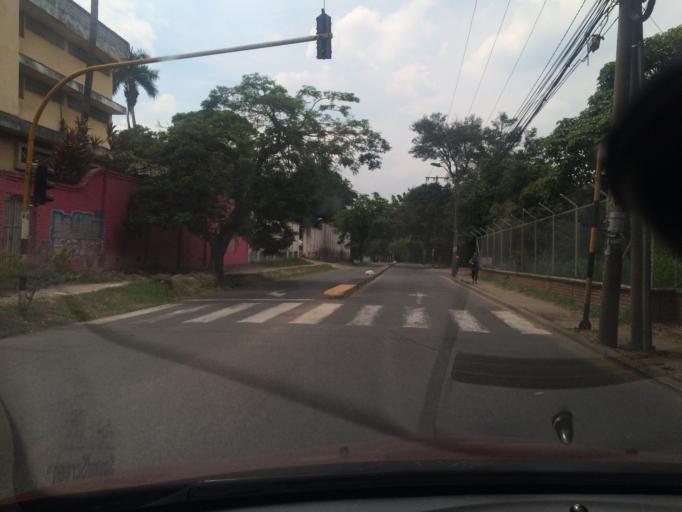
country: CO
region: Valle del Cauca
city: Cali
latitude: 3.4294
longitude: -76.5469
